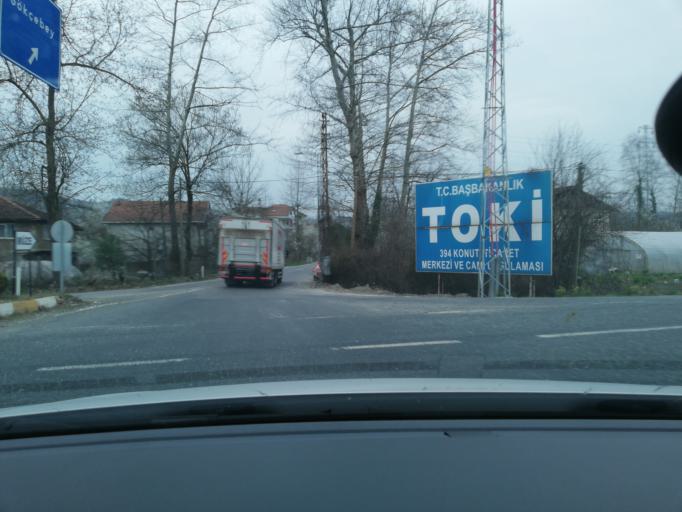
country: TR
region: Zonguldak
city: Gokcebey
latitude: 41.2999
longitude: 32.1199
